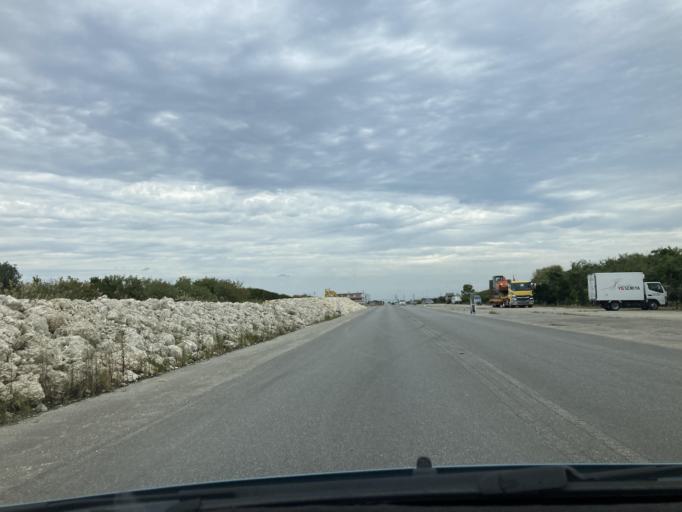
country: JP
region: Okinawa
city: Okinawa
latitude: 26.3884
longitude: 127.7463
